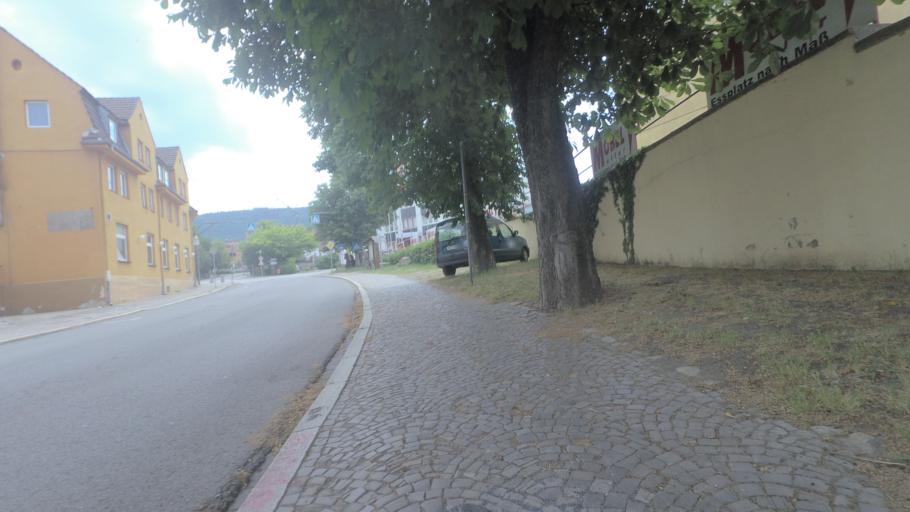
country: DE
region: Saxony-Anhalt
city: Thale
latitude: 51.7485
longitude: 11.0327
